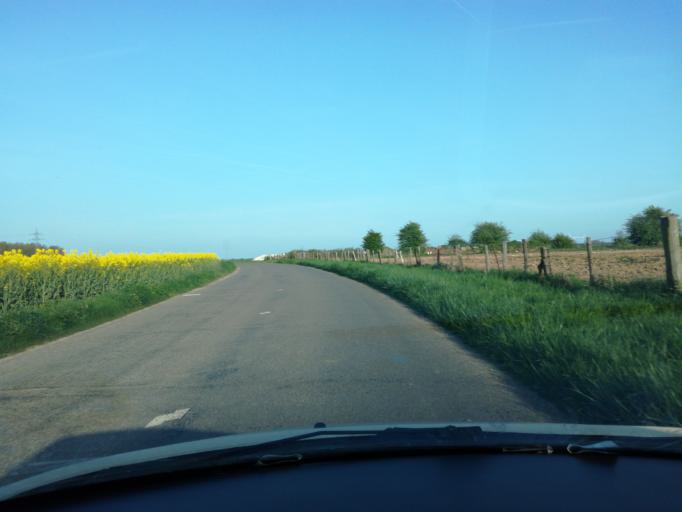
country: FR
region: Picardie
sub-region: Departement de la Somme
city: Poix-de-Picardie
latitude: 49.8179
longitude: 1.9681
